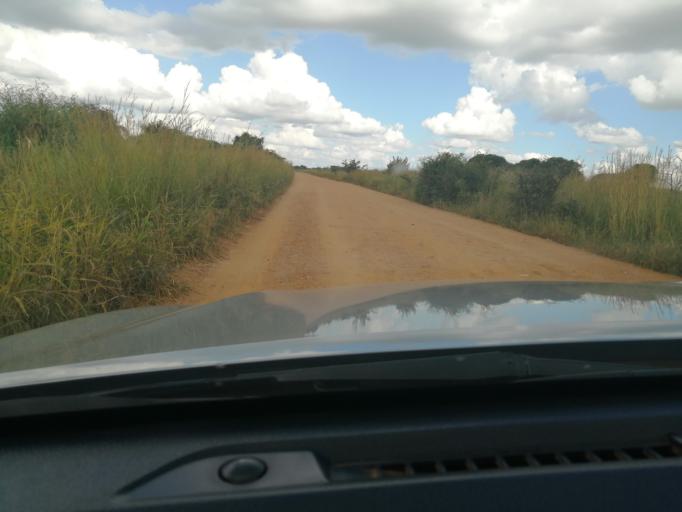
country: ZM
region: Lusaka
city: Lusaka
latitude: -15.2091
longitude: 28.0876
